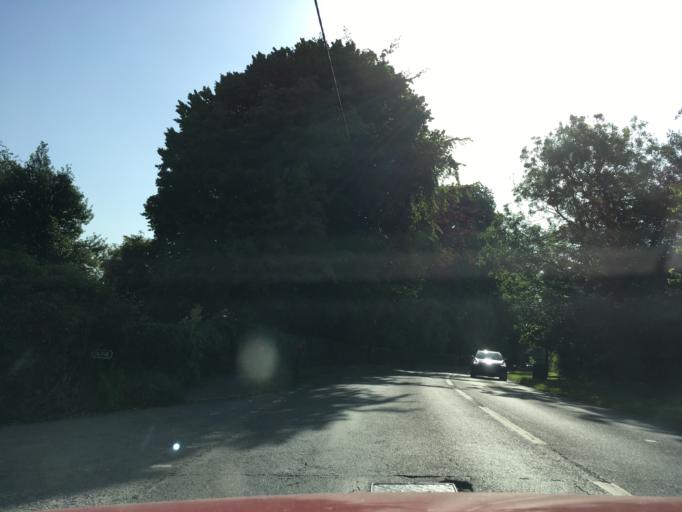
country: GB
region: England
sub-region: Oxfordshire
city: Deddington
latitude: 51.9281
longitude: -1.3721
